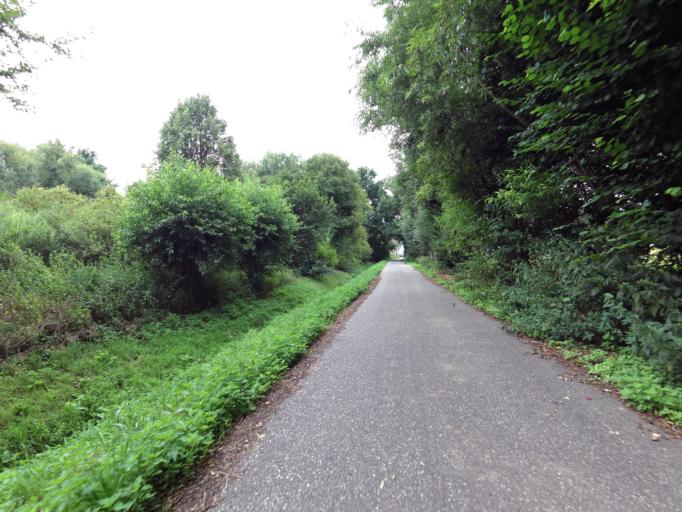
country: DE
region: North Rhine-Westphalia
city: Geilenkirchen
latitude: 50.9944
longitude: 6.1629
